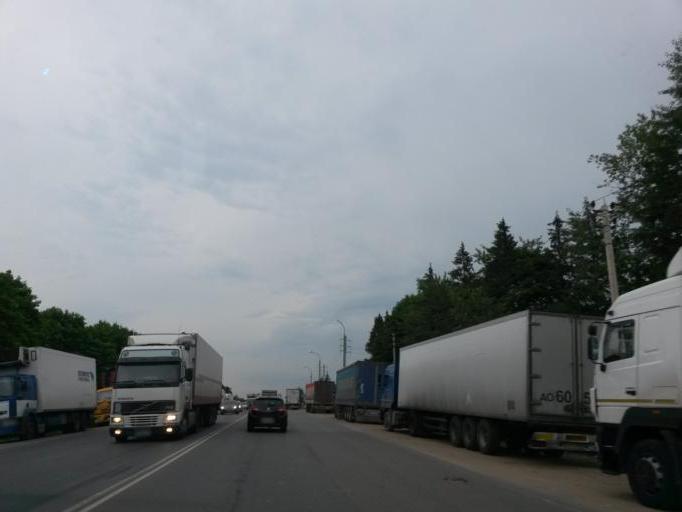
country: RU
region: Moskovskaya
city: Yam
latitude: 55.4752
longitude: 37.7138
